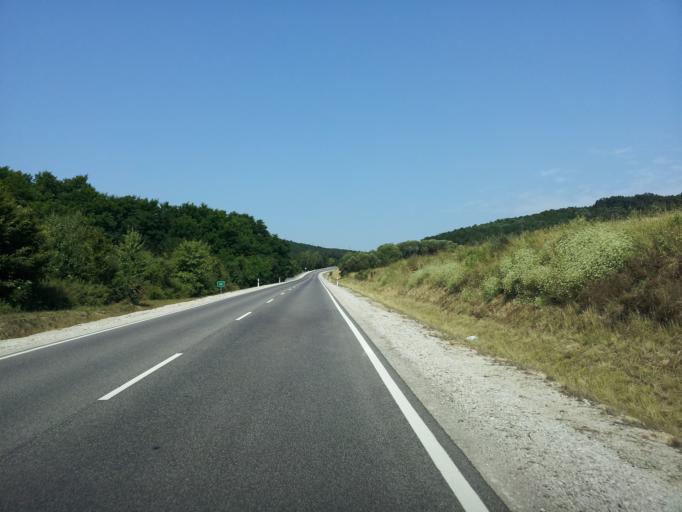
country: HU
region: Zala
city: Pacsa
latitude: 46.8094
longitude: 17.0669
